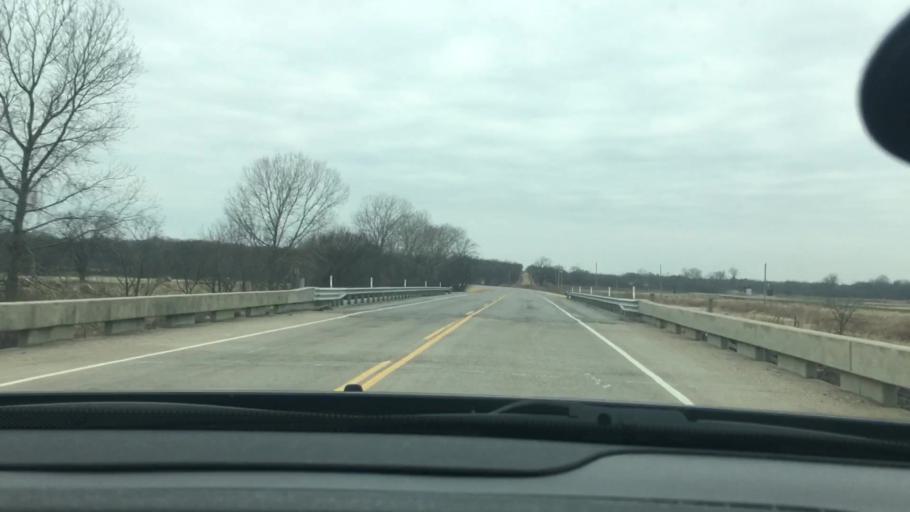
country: US
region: Oklahoma
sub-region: Carter County
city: Healdton
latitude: 34.4925
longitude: -97.4398
